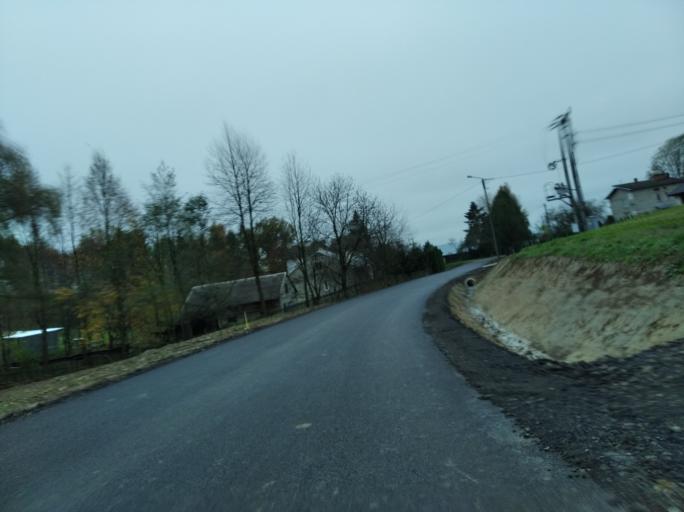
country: PL
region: Subcarpathian Voivodeship
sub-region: Powiat krosnienski
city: Odrzykon
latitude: 49.7345
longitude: 21.7721
